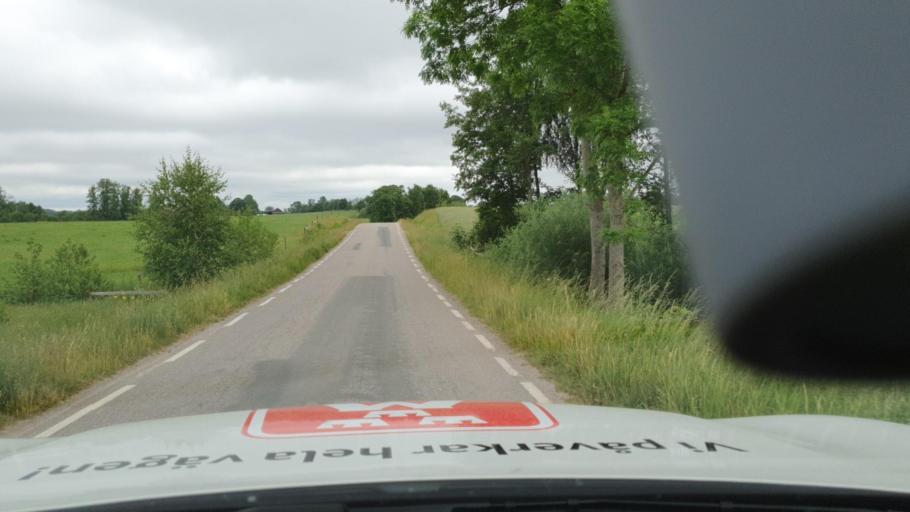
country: SE
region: Vaestra Goetaland
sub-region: Tibro Kommun
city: Tibro
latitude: 58.3757
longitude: 14.1768
